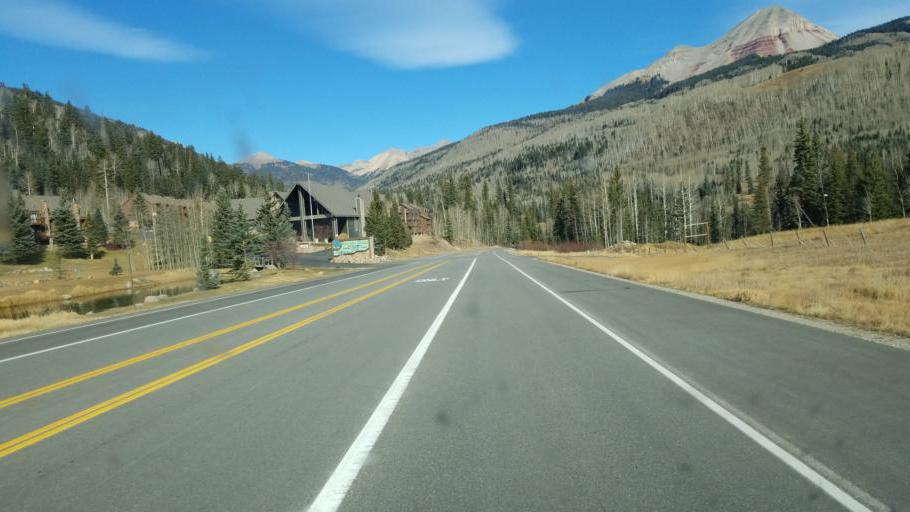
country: US
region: Colorado
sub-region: San Juan County
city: Silverton
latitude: 37.6530
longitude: -107.8096
